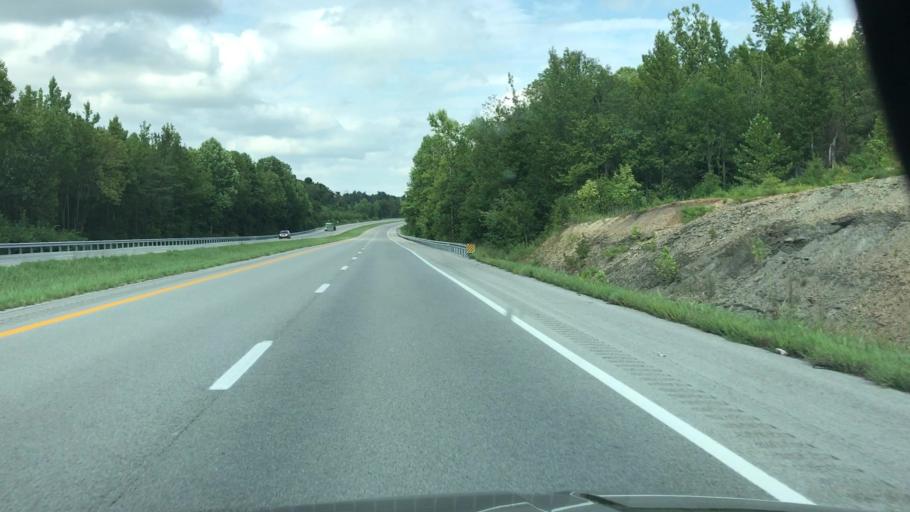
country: US
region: Kentucky
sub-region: Hopkins County
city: Dawson Springs
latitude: 37.1612
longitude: -87.7617
